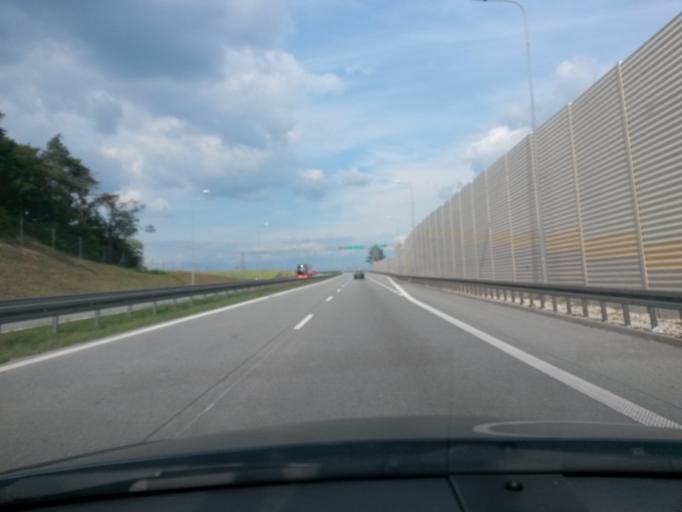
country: PL
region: Lodz Voivodeship
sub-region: Powiat skierniewicki
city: Kowiesy
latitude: 51.8420
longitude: 20.3554
